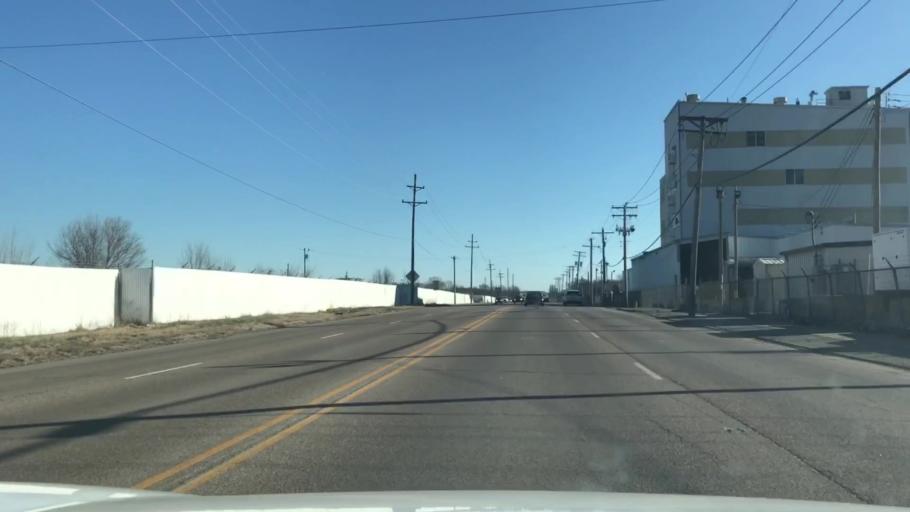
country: US
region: Illinois
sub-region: Saint Clair County
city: Alorton
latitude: 38.5994
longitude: -90.1273
